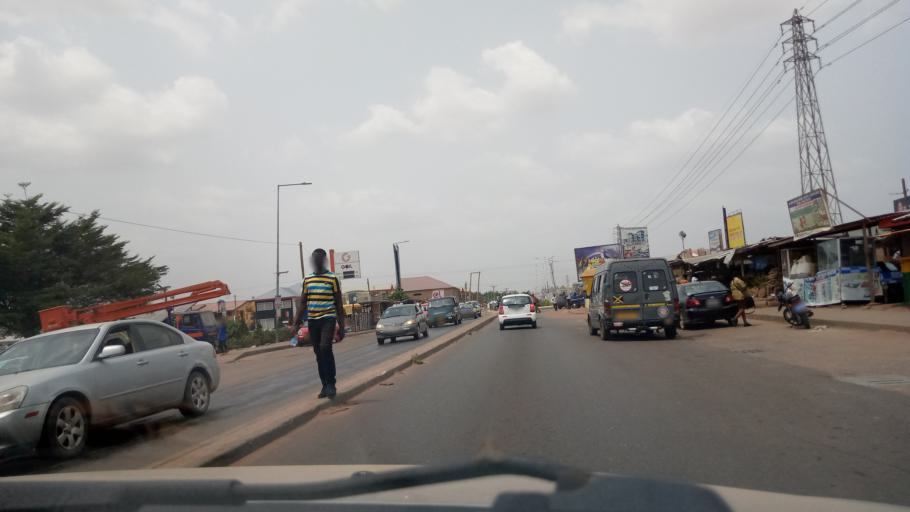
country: GH
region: Greater Accra
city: Dome
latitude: 5.6677
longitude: -0.2380
